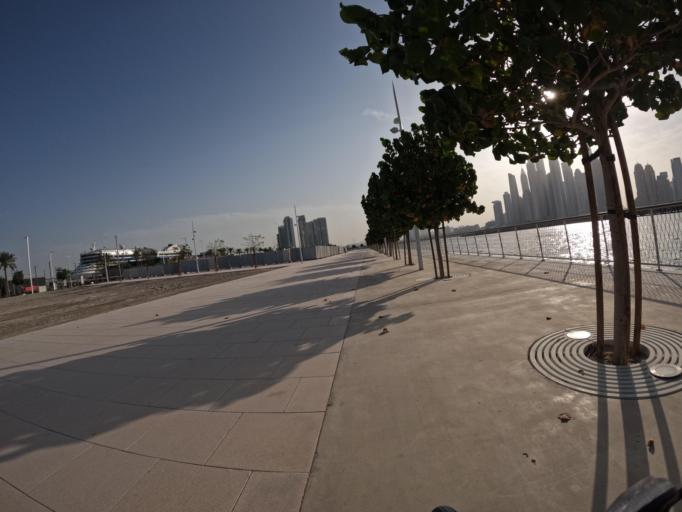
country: AE
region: Dubai
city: Dubai
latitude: 25.0916
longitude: 55.1308
